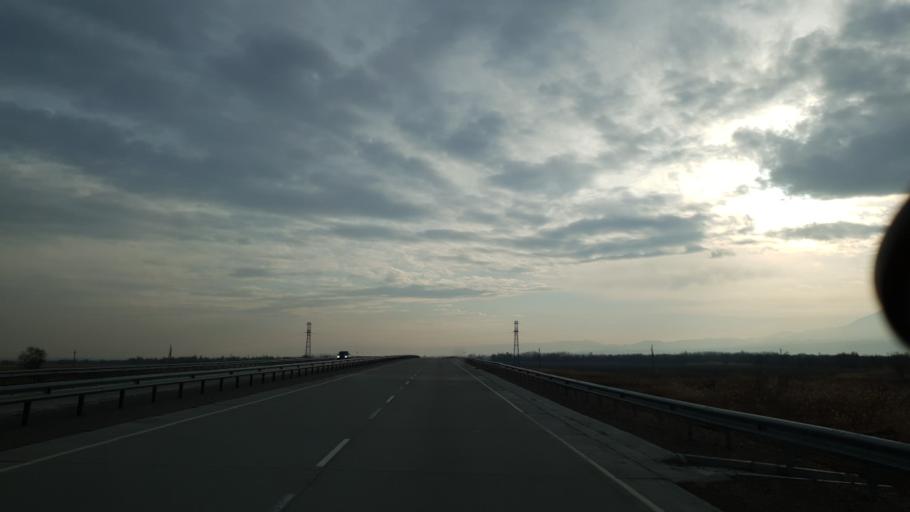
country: KZ
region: Almaty Oblysy
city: Turgen'
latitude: 43.5797
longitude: 78.0695
